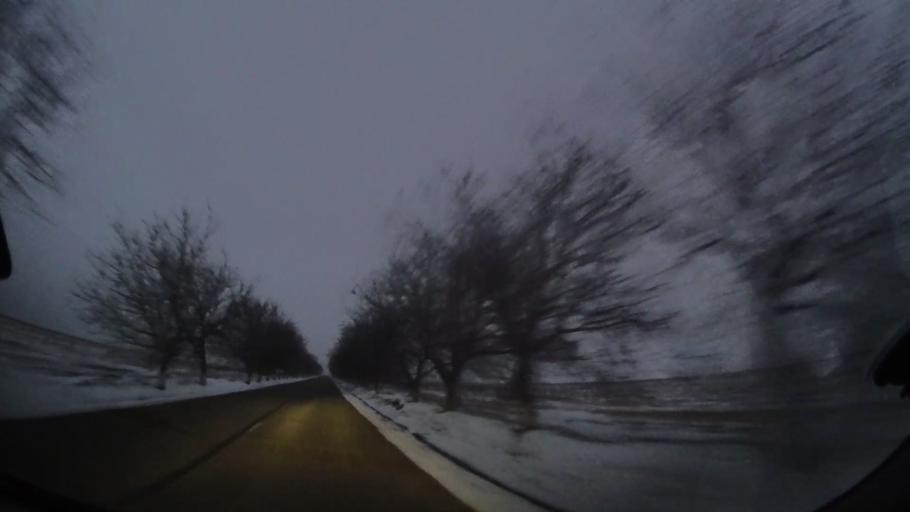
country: RO
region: Vaslui
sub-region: Comuna Dimitrie Cantemir
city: Dimitrie Cantemir
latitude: 46.5192
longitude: 28.0280
